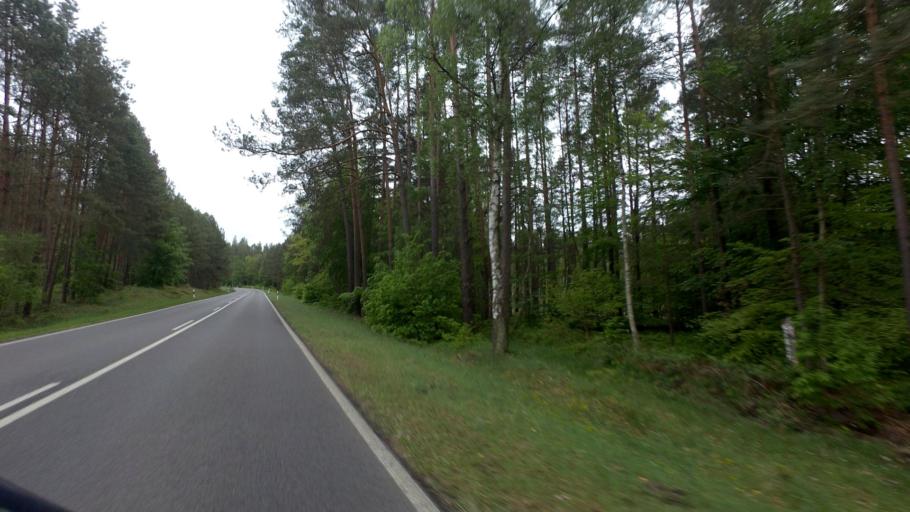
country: DE
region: Brandenburg
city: Lychen
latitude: 53.1767
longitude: 13.3326
